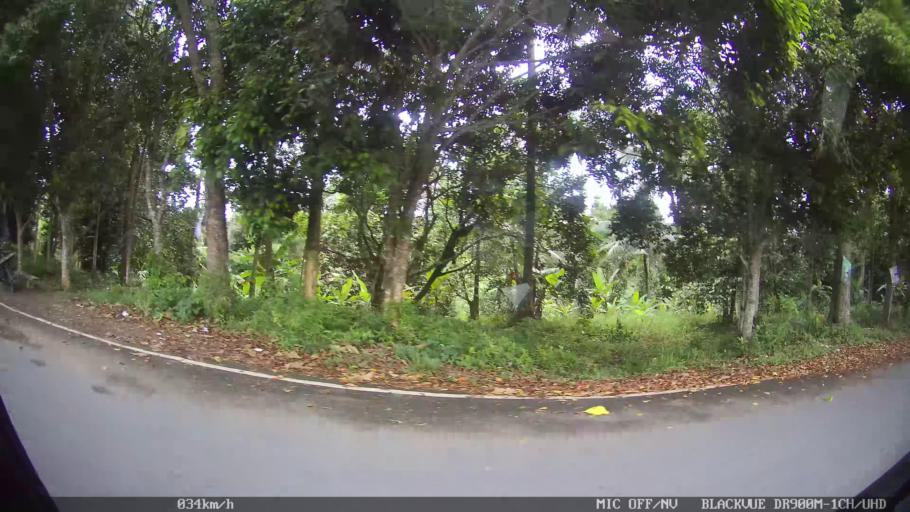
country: ID
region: Lampung
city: Bandarlampung
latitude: -5.4305
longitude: 105.2053
